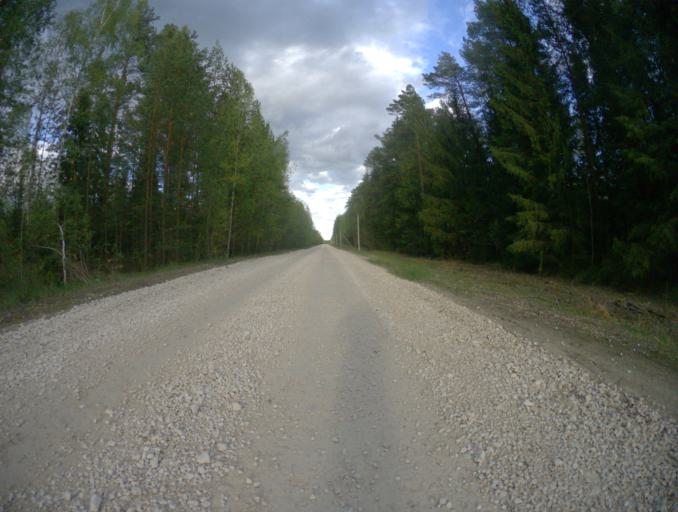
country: RU
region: Vladimir
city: Gusevskiy
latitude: 55.7210
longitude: 40.5847
